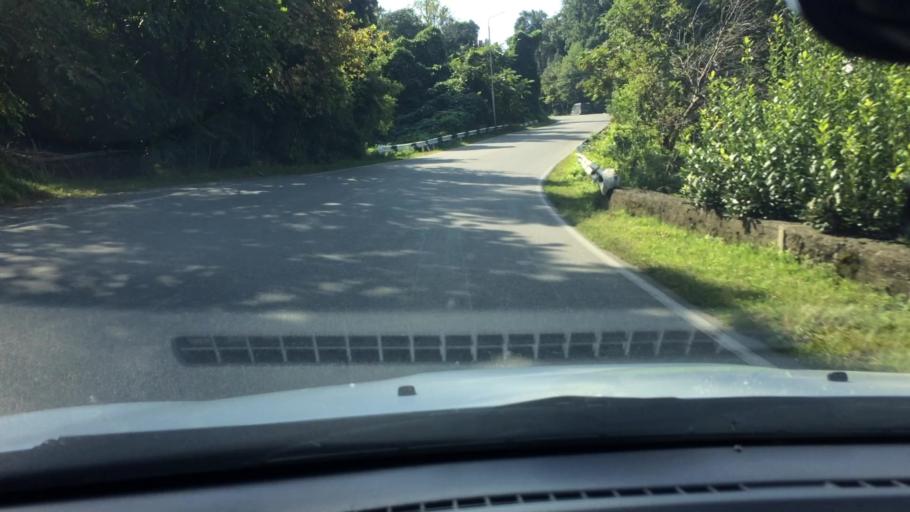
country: GE
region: Ajaria
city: Kobuleti
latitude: 41.7700
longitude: 41.7556
